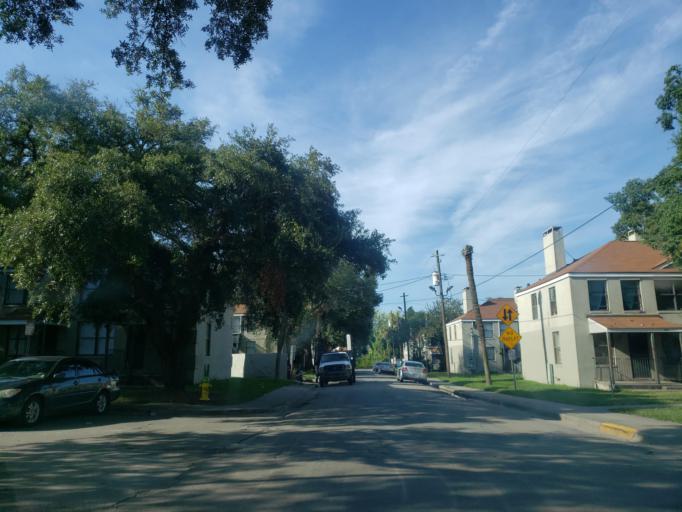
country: US
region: Georgia
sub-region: Chatham County
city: Savannah
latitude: 32.0814
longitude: -81.1018
